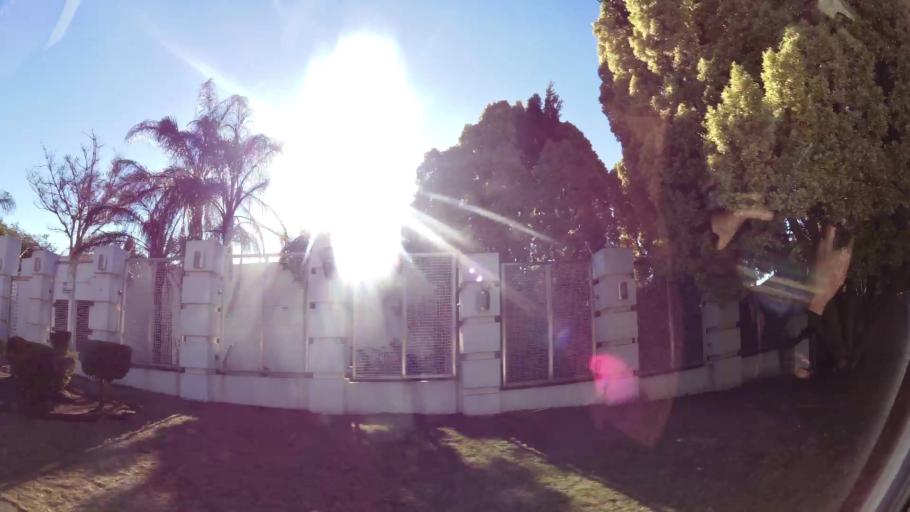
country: ZA
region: Limpopo
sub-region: Capricorn District Municipality
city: Polokwane
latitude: -23.8825
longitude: 29.4907
